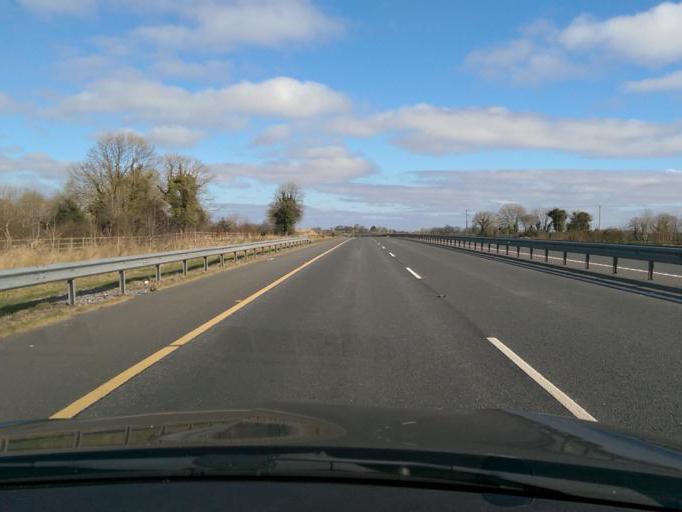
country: IE
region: Leinster
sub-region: An Iarmhi
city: Athlone
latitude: 53.3685
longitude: -8.0583
